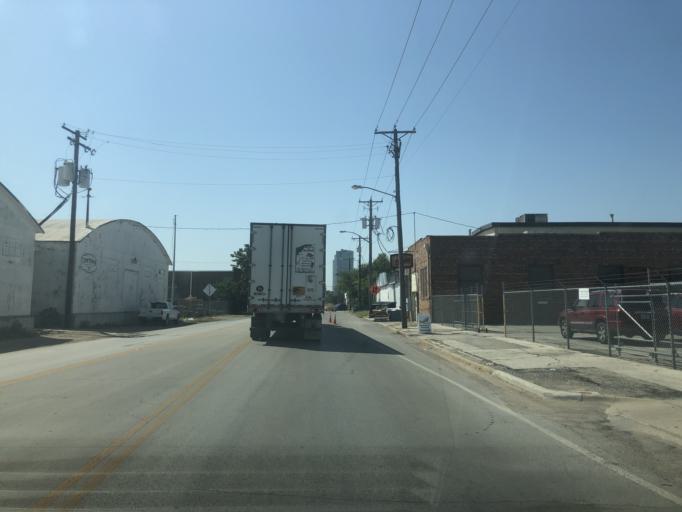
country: US
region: Texas
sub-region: Tarrant County
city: Fort Worth
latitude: 32.7700
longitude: -97.3405
